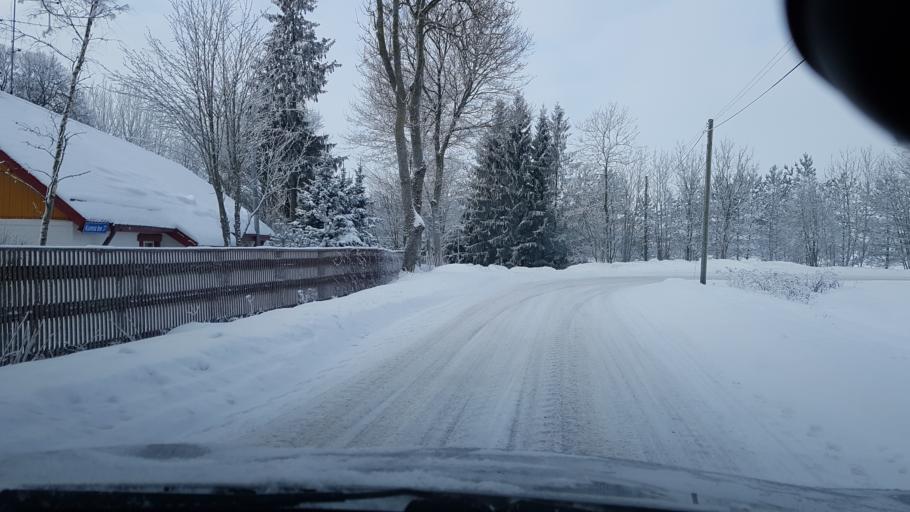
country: EE
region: Harju
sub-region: Keila linn
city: Keila
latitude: 59.3323
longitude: 24.4436
